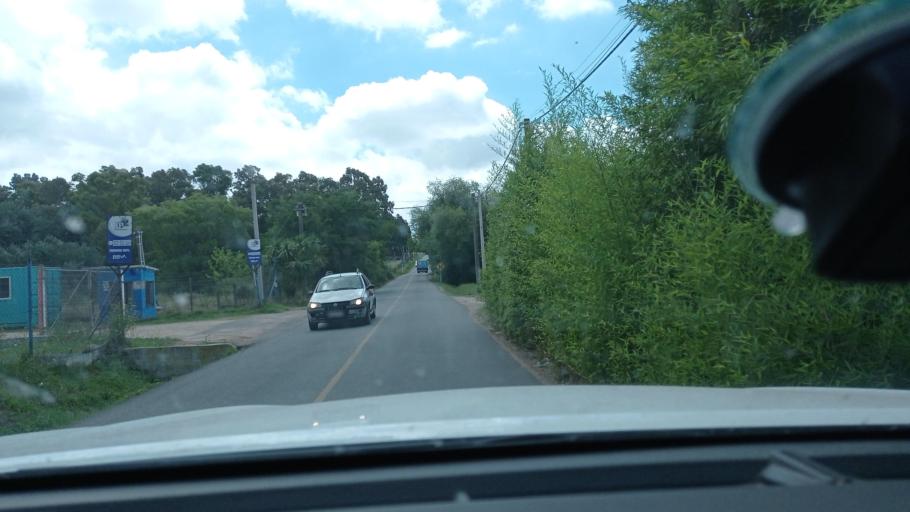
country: UY
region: Canelones
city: La Paz
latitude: -34.8104
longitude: -56.1949
